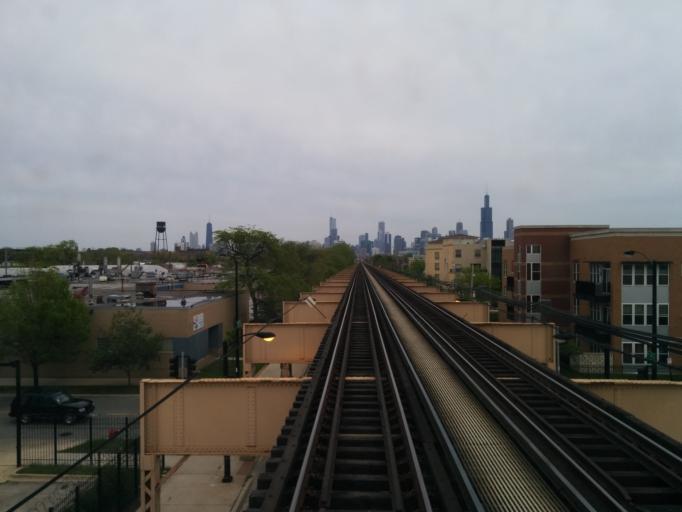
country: US
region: Illinois
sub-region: Cook County
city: Chicago
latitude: 41.8847
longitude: -87.6844
